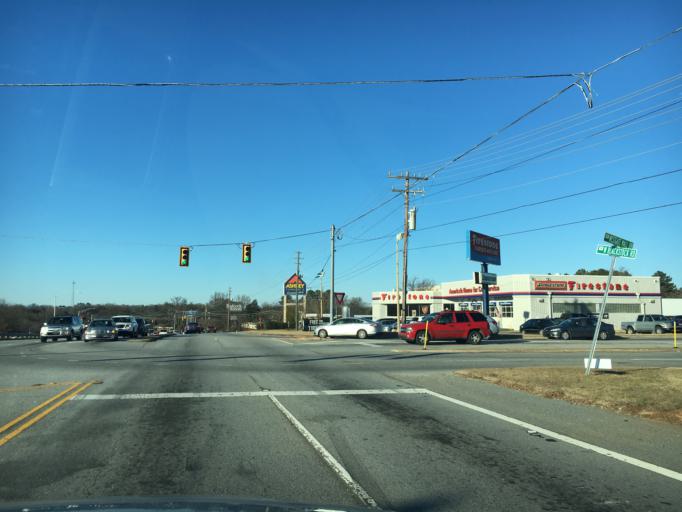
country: US
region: South Carolina
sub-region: Spartanburg County
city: Arcadia
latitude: 34.9398
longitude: -81.9912
